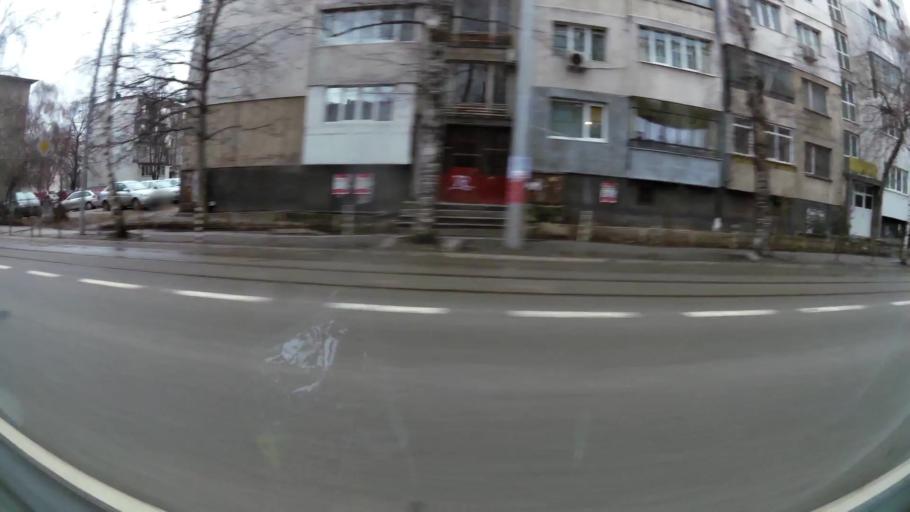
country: BG
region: Sofia-Capital
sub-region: Stolichna Obshtina
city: Sofia
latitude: 42.7348
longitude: 23.3073
